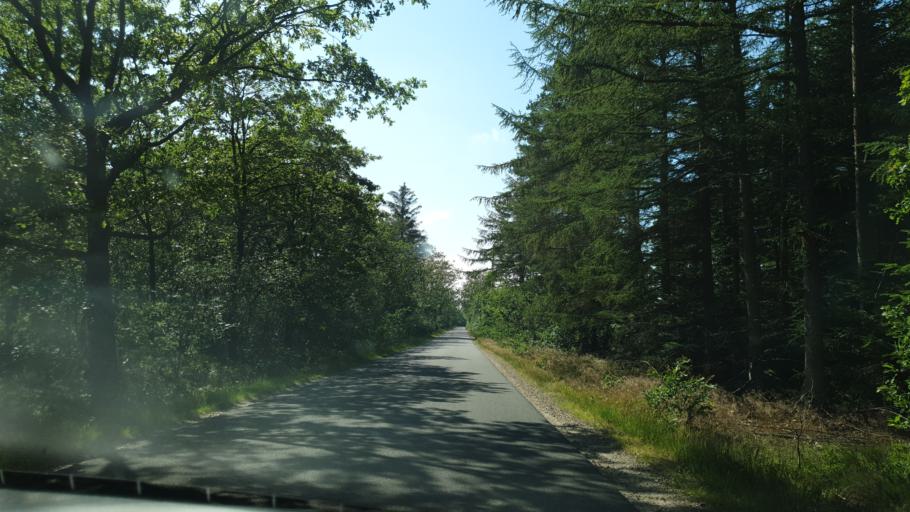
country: DK
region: Central Jutland
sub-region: Ringkobing-Skjern Kommune
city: Skjern
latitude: 55.9993
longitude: 8.4380
